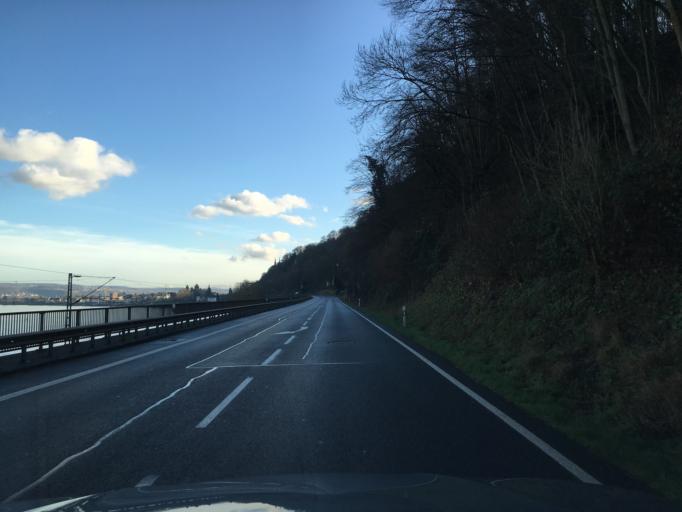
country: DE
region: Rheinland-Pfalz
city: Unkel
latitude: 50.5881
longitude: 7.2119
